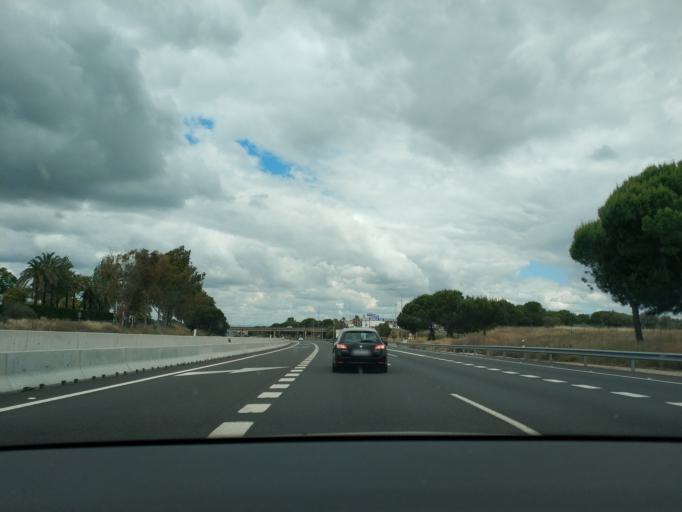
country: ES
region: Andalusia
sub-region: Provincia de Sevilla
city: Benacazon
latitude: 37.3603
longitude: -6.1968
